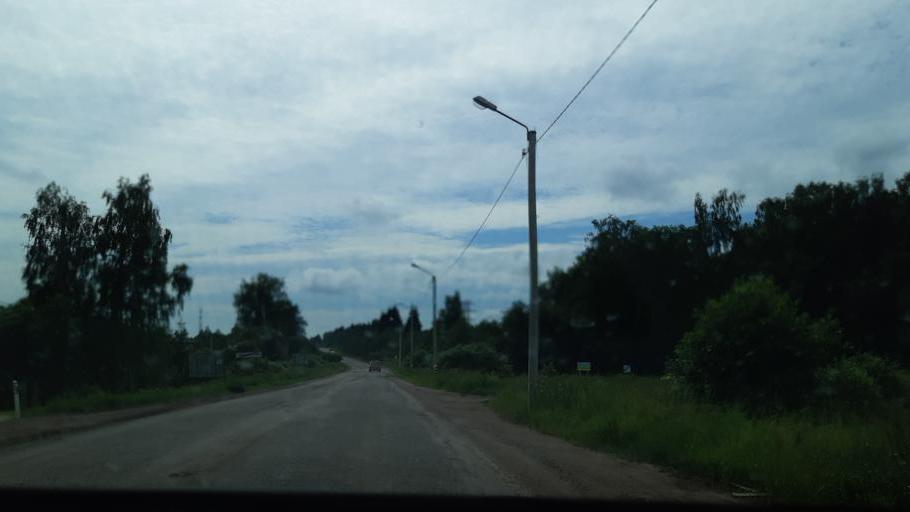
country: RU
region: Moskovskaya
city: Vereya
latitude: 55.3341
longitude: 36.1565
